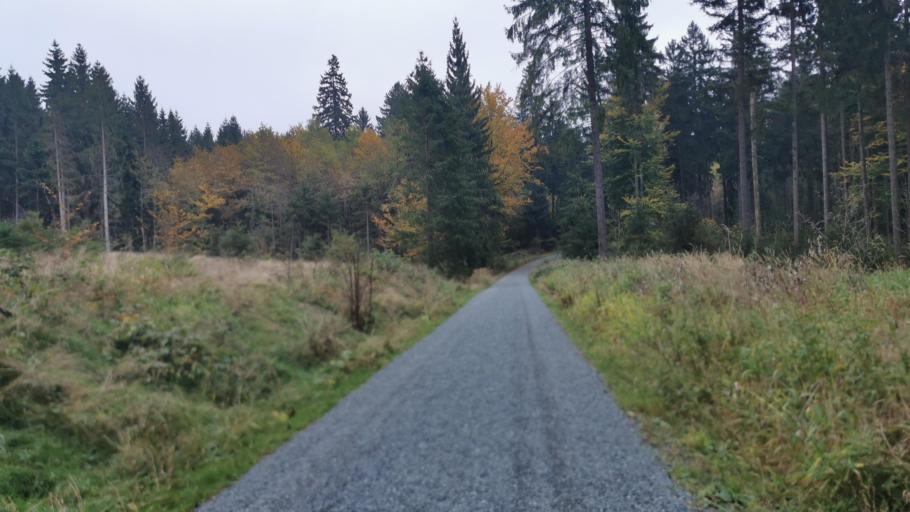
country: DE
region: Bavaria
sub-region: Upper Franconia
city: Ludwigsstadt
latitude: 50.4446
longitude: 11.3554
